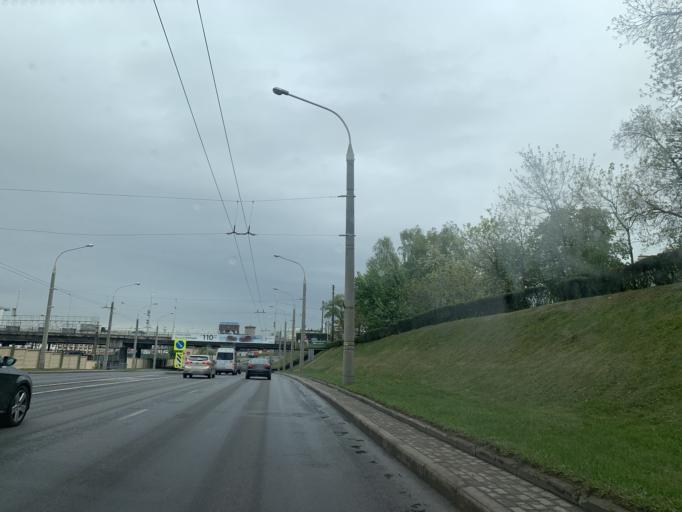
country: BY
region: Minsk
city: Syenitsa
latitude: 53.8730
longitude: 27.5256
